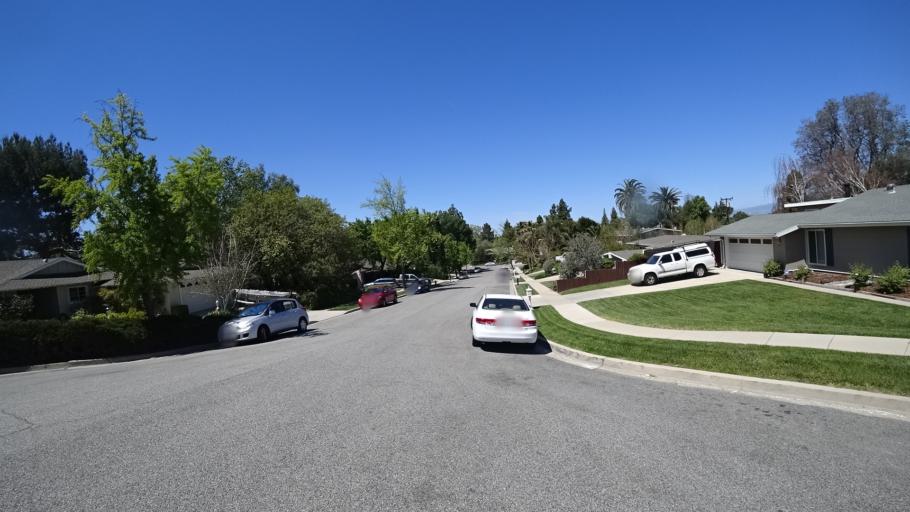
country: US
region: California
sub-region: Ventura County
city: Thousand Oaks
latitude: 34.1914
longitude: -118.8450
